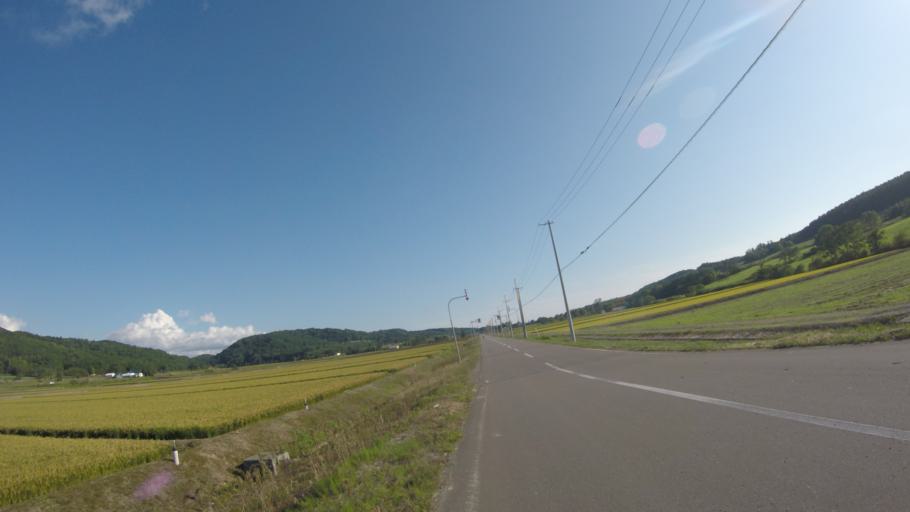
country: JP
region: Hokkaido
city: Iwamizawa
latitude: 43.1986
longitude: 141.8258
